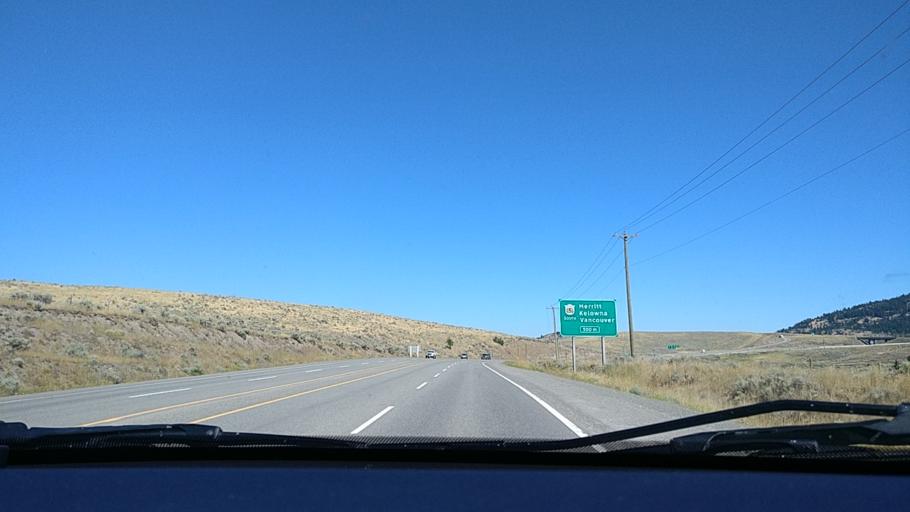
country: CA
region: British Columbia
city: Kamloops
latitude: 50.6688
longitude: -120.4730
